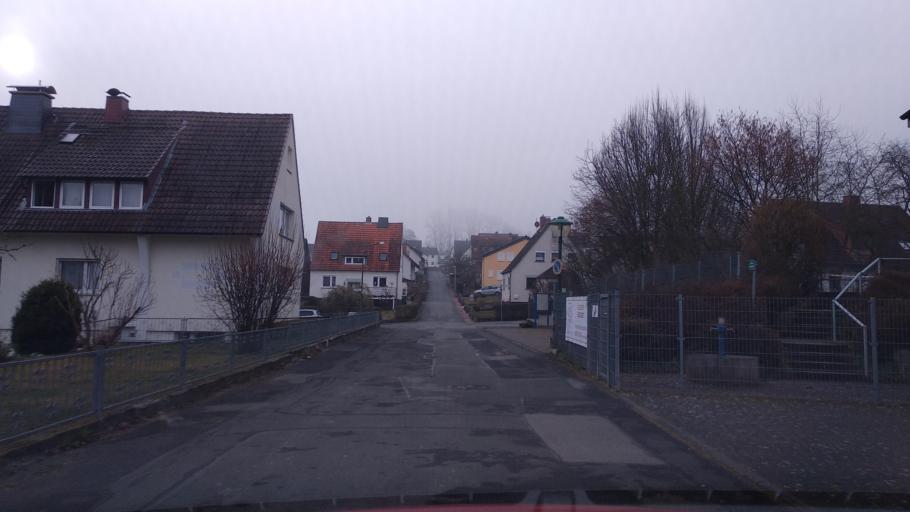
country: DE
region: Hesse
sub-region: Regierungsbezirk Kassel
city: Calden
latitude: 51.3622
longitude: 9.3826
